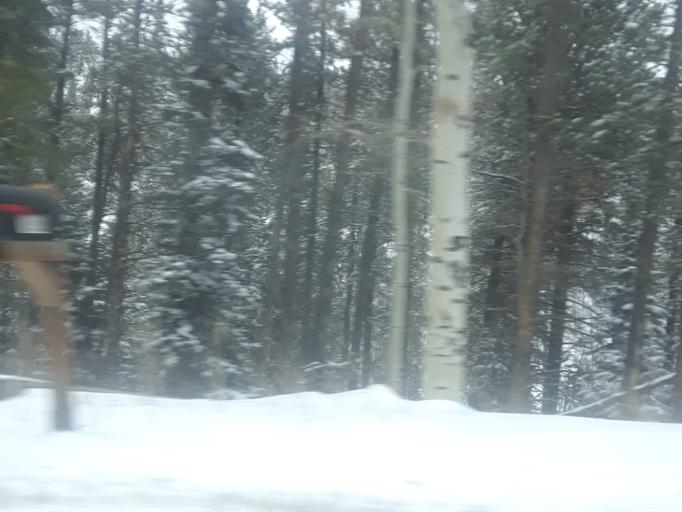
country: US
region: Colorado
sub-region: Boulder County
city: Coal Creek
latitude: 39.9255
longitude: -105.4091
